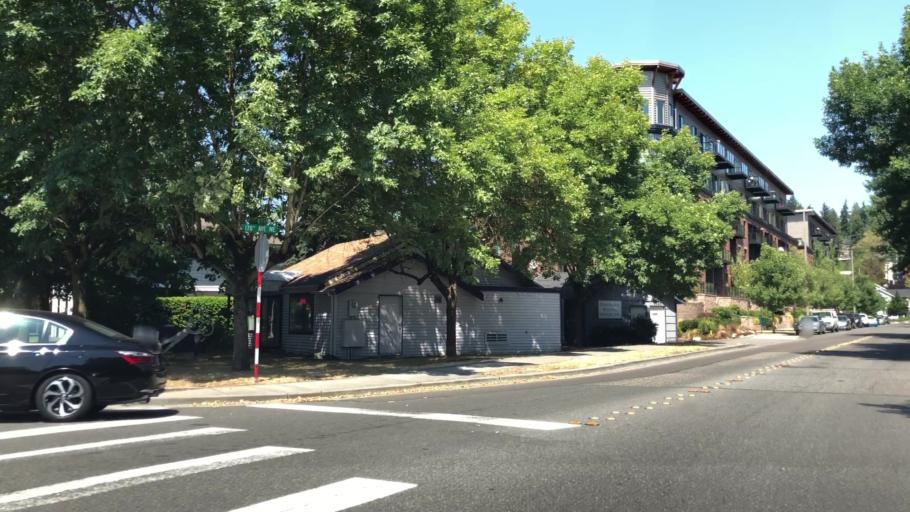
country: US
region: Washington
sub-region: King County
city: Redmond
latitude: 47.6730
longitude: -122.1139
